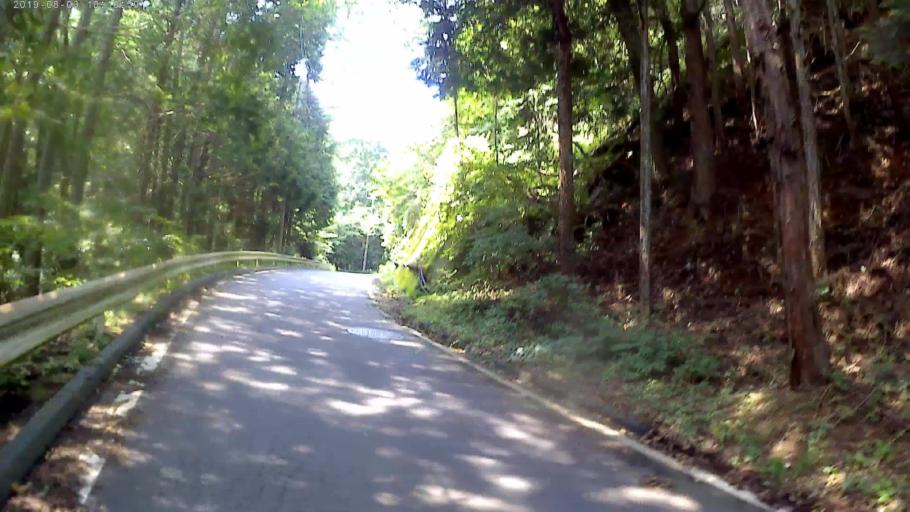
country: JP
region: Yamanashi
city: Enzan
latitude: 35.6335
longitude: 138.7682
